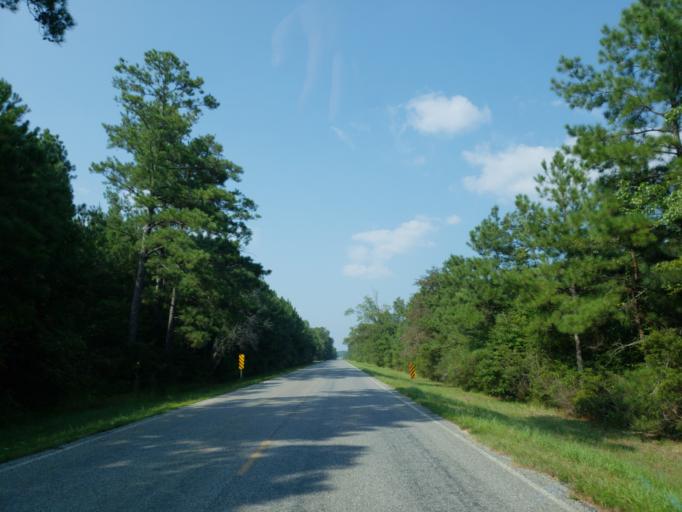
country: US
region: Mississippi
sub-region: Clarke County
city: Stonewall
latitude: 32.0246
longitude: -88.8891
